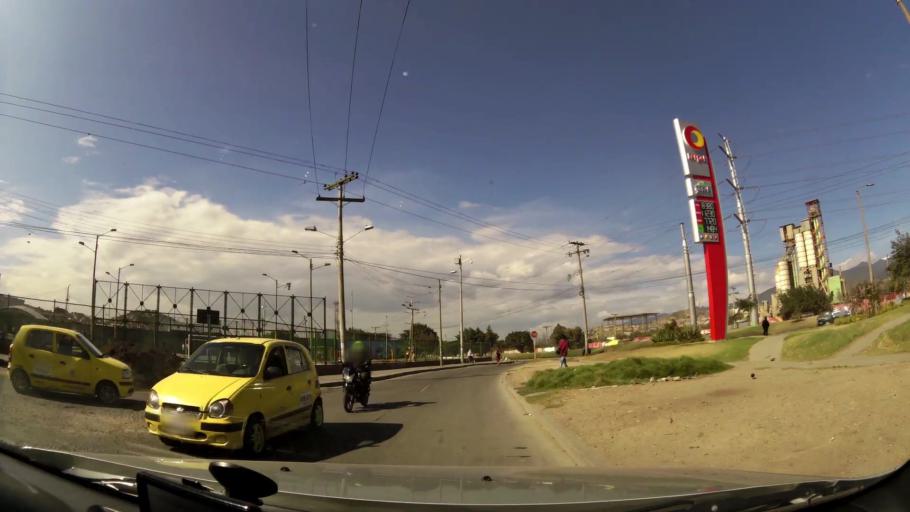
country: CO
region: Bogota D.C.
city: Bogota
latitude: 4.5470
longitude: -74.1375
